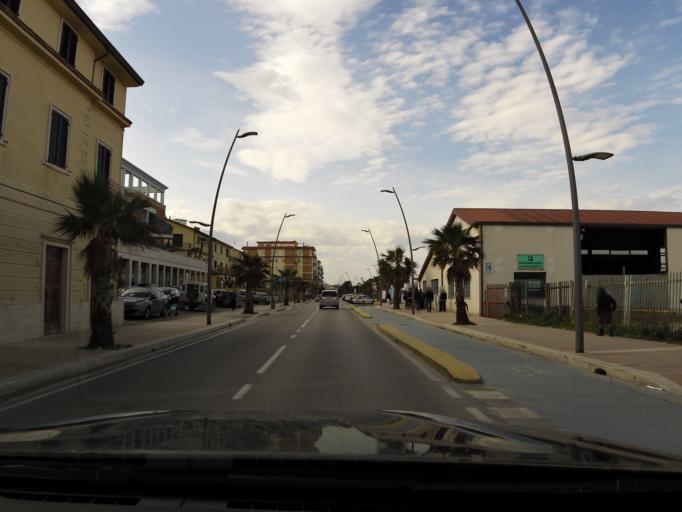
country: IT
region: The Marches
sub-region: Provincia di Macerata
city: Portocivitanova
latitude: 43.3128
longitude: 13.7266
